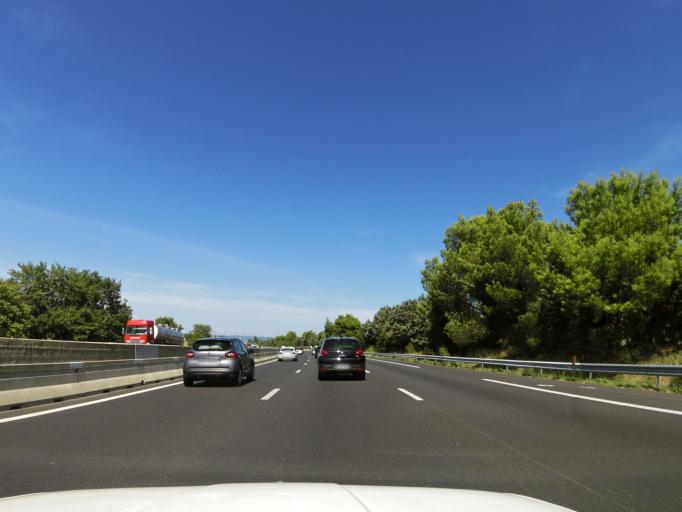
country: FR
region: Provence-Alpes-Cote d'Azur
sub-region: Departement du Vaucluse
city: Bollene
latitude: 44.3084
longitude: 4.7468
